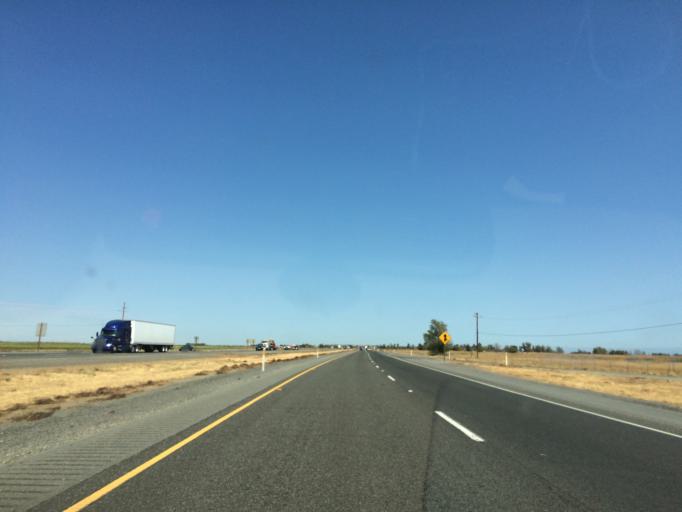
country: US
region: California
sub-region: Glenn County
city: Willows
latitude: 39.4087
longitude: -122.1956
